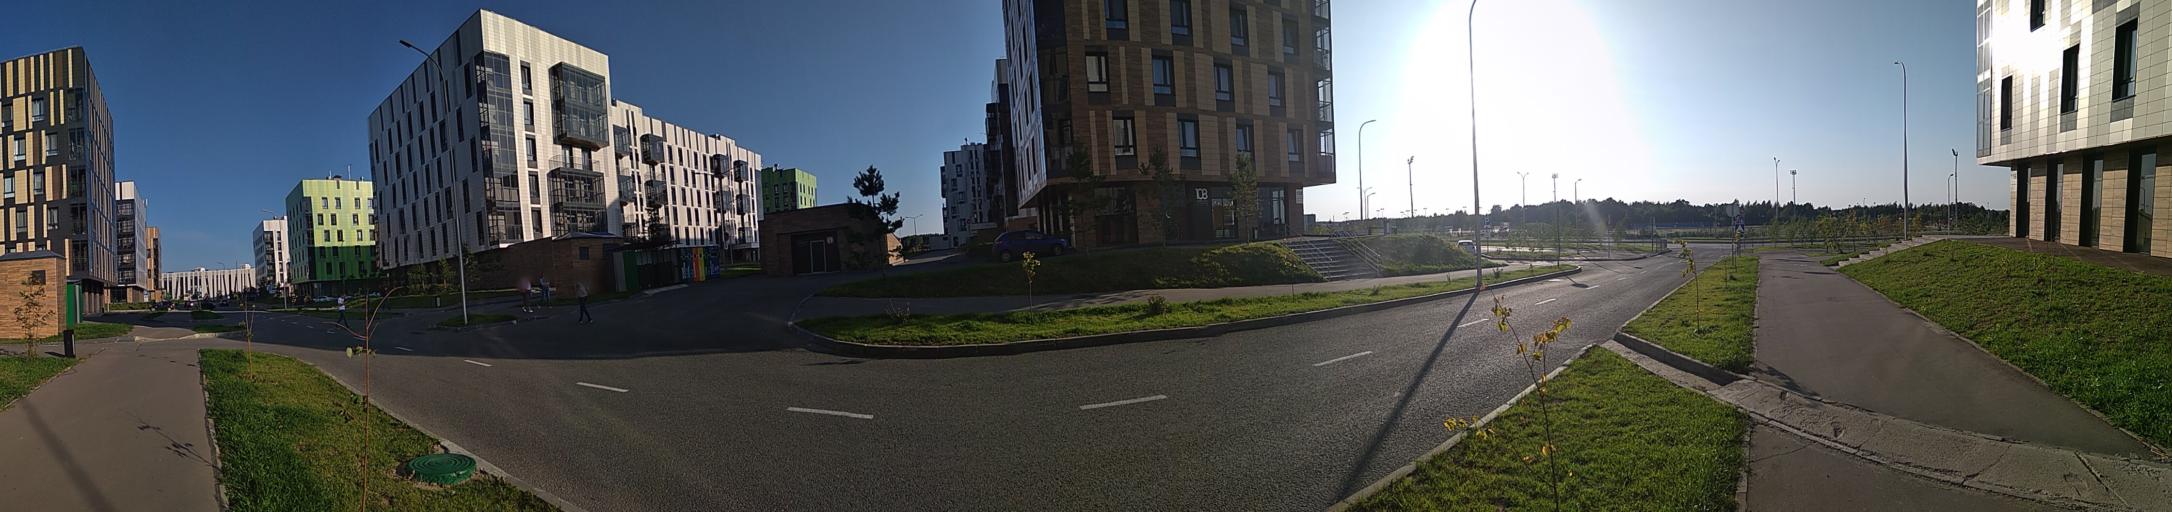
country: RU
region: Tatarstan
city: Sviyazhsk
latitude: 55.7451
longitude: 48.7410
